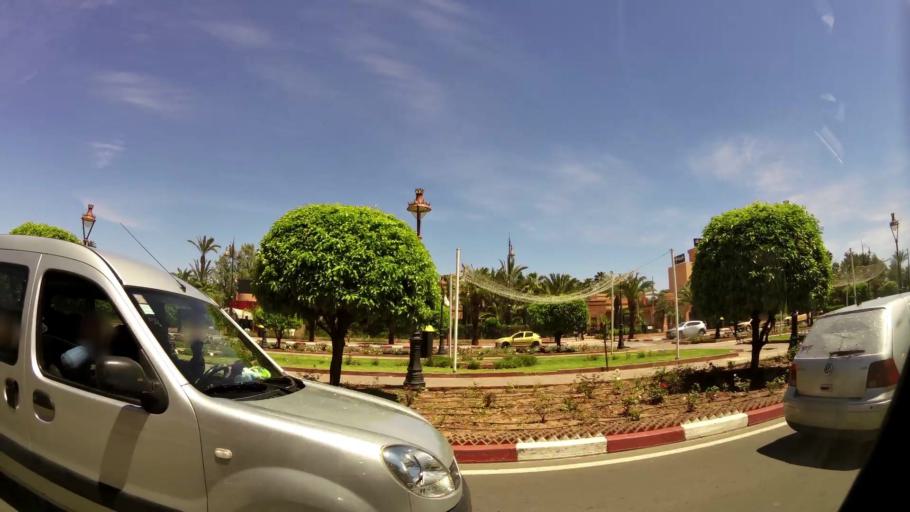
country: MA
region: Marrakech-Tensift-Al Haouz
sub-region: Marrakech
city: Marrakesh
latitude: 31.6190
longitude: -8.0091
